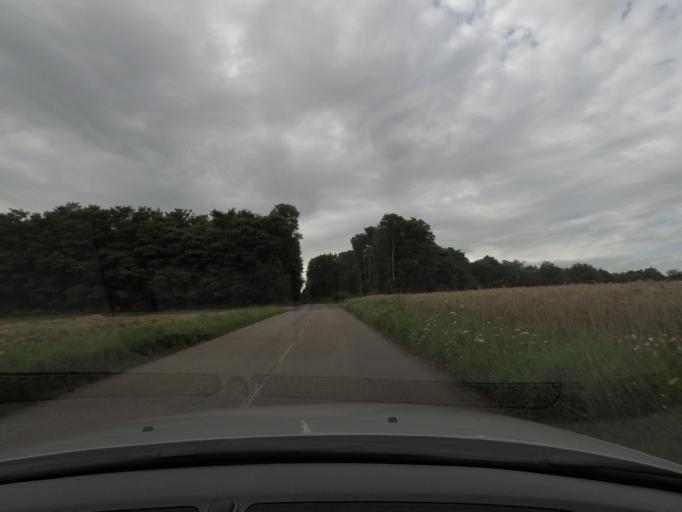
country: FR
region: Haute-Normandie
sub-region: Departement de l'Eure
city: Le Manoir
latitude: 49.3314
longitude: 1.2068
